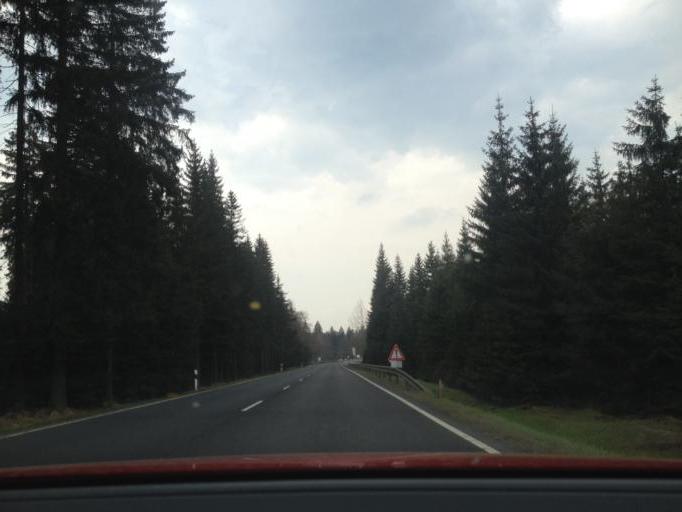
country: DE
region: Bavaria
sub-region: Upper Franconia
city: Fichtelberg
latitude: 50.0352
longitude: 11.8436
